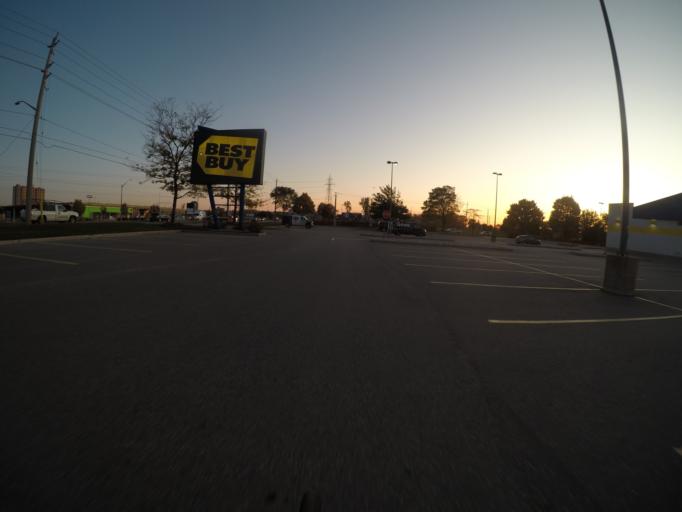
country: CA
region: Ontario
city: Kitchener
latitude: 43.4218
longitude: -80.4380
